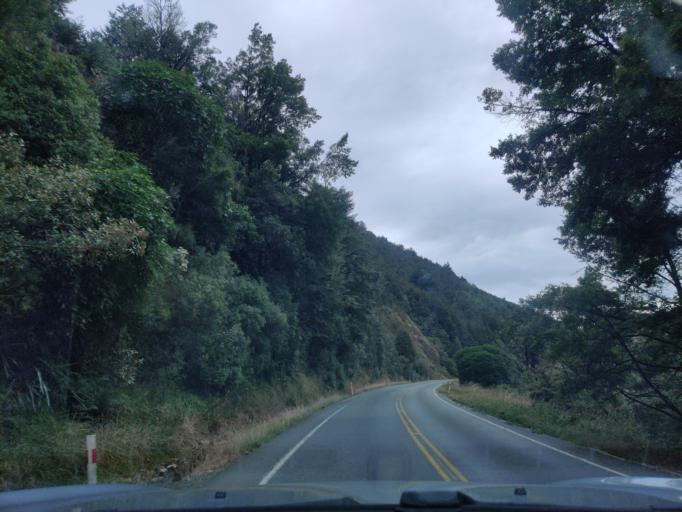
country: NZ
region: Tasman
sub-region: Tasman District
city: Wakefield
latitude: -41.6969
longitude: 172.6186
